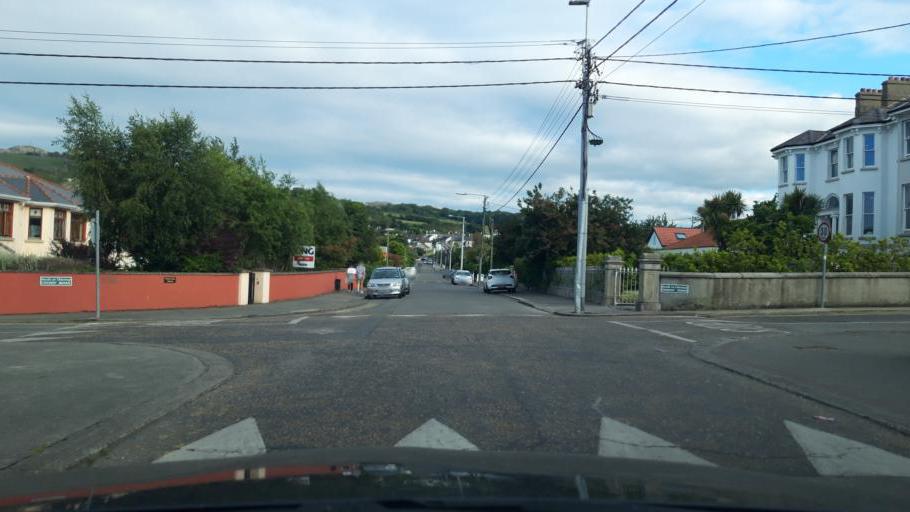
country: IE
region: Leinster
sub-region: Wicklow
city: Bray
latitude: 53.1984
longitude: -6.1007
